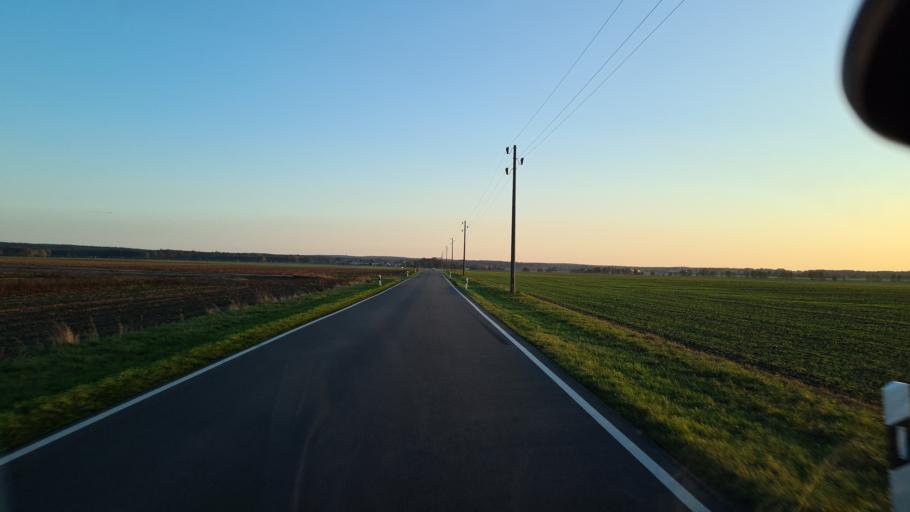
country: DE
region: Saxony
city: Torgau
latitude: 51.4897
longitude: 13.0026
